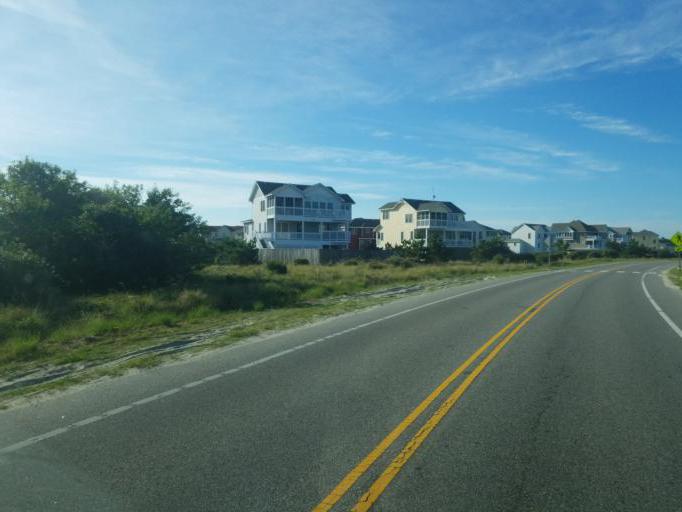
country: US
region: North Carolina
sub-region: Currituck County
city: Currituck
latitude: 36.3879
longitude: -75.8306
